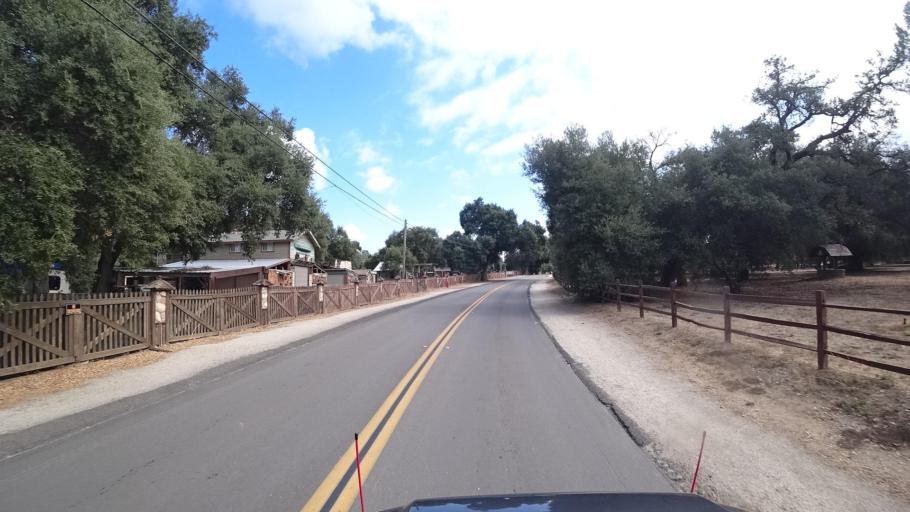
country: US
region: California
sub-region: San Diego County
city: Campo
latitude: 32.6824
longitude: -116.5158
